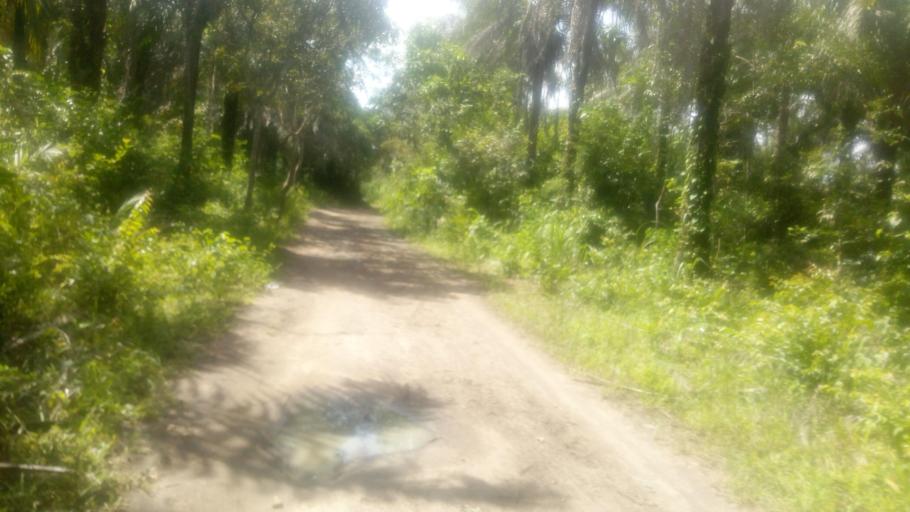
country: SL
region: Northern Province
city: Magburaka
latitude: 8.6592
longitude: -12.0691
